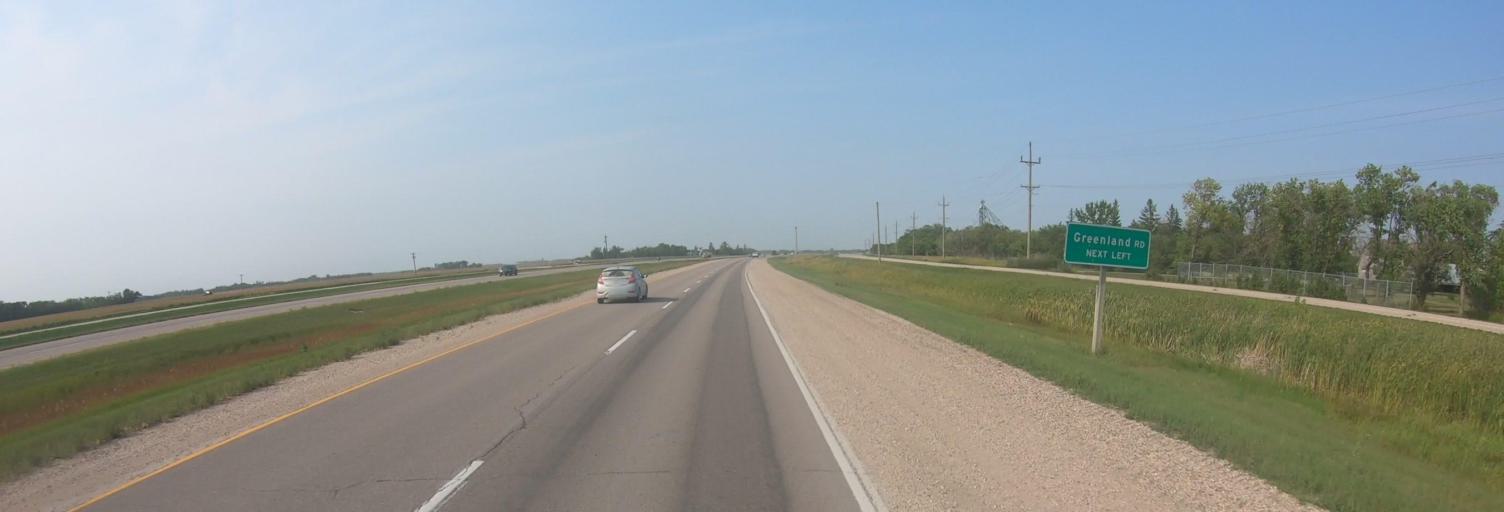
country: CA
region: Manitoba
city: Steinbach
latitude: 49.6314
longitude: -96.6865
